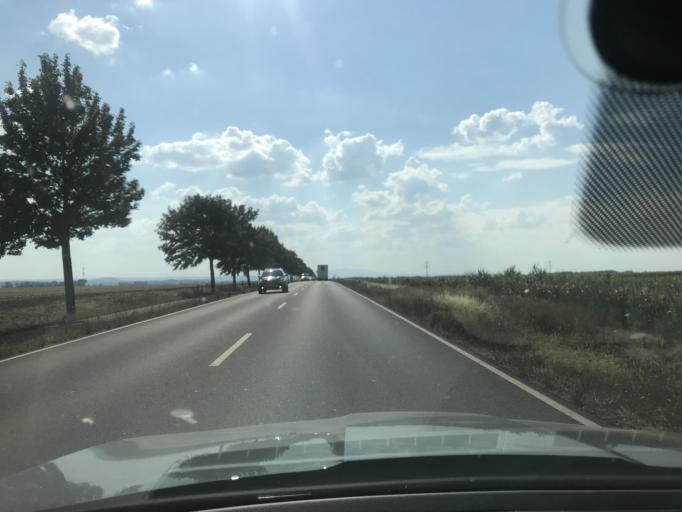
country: DE
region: Saxony-Anhalt
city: Gross Quenstedt
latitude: 51.9163
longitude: 11.1319
